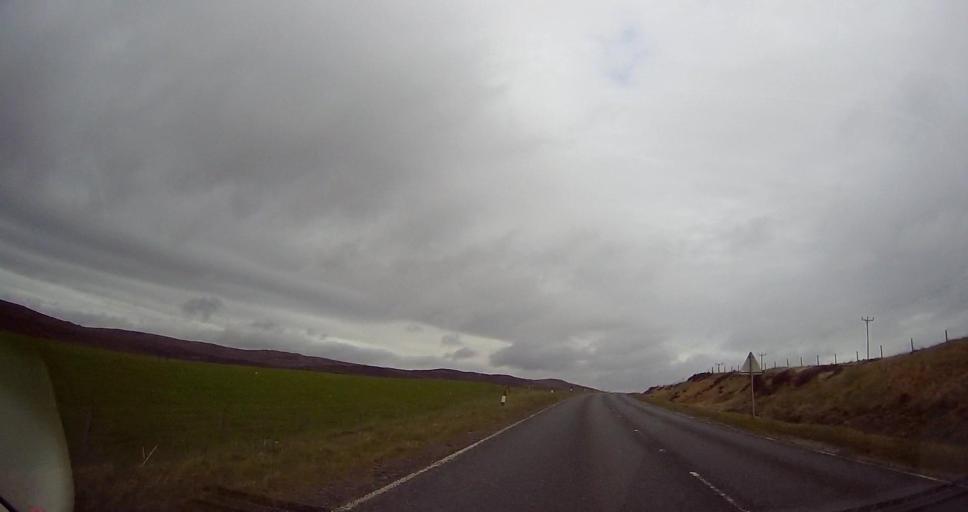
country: GB
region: Scotland
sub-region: Shetland Islands
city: Lerwick
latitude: 60.1998
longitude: -1.2326
